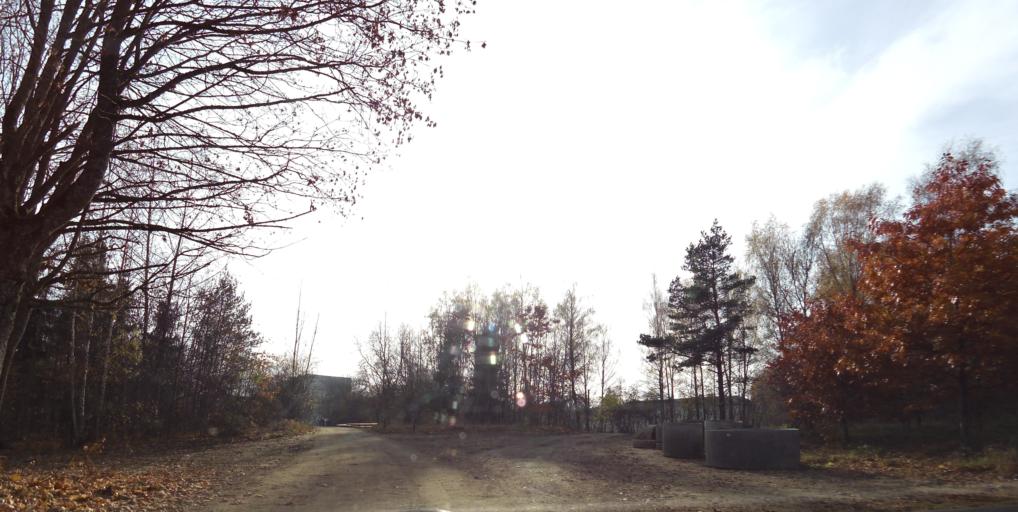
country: LT
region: Vilnius County
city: Pilaite
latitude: 54.7197
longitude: 25.1943
